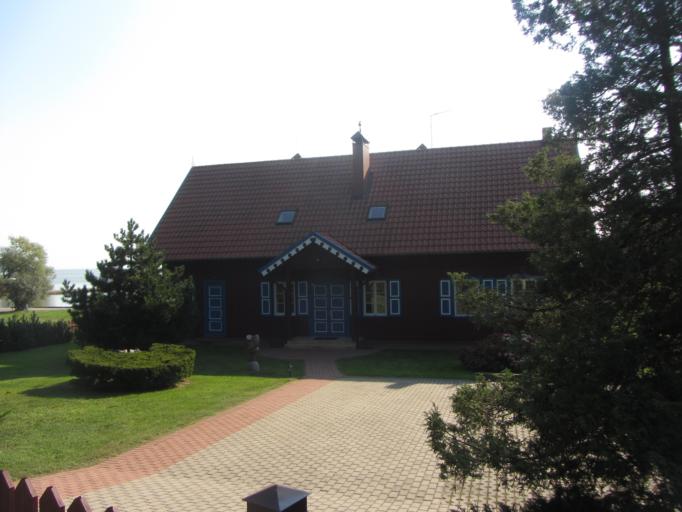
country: LT
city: Nida
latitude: 55.3091
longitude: 21.0085
